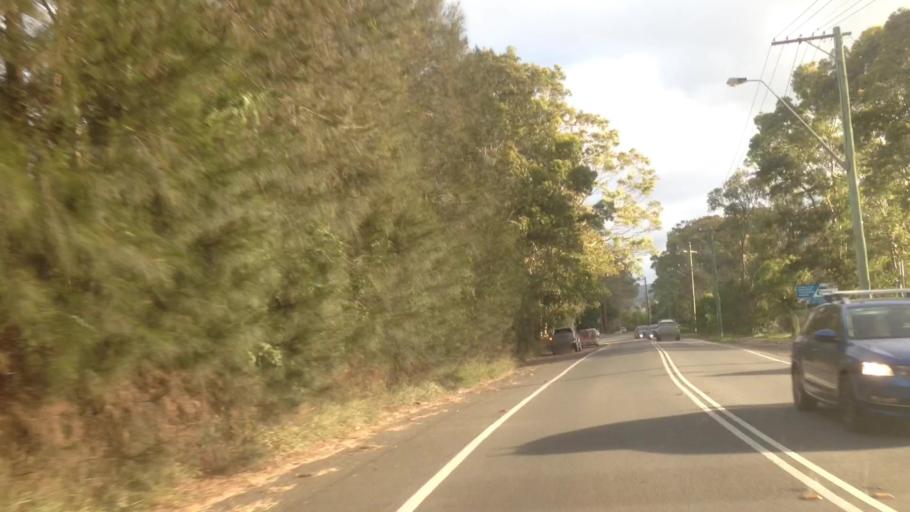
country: AU
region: New South Wales
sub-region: Wyong Shire
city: Chittaway Bay
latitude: -33.2874
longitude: 151.4244
